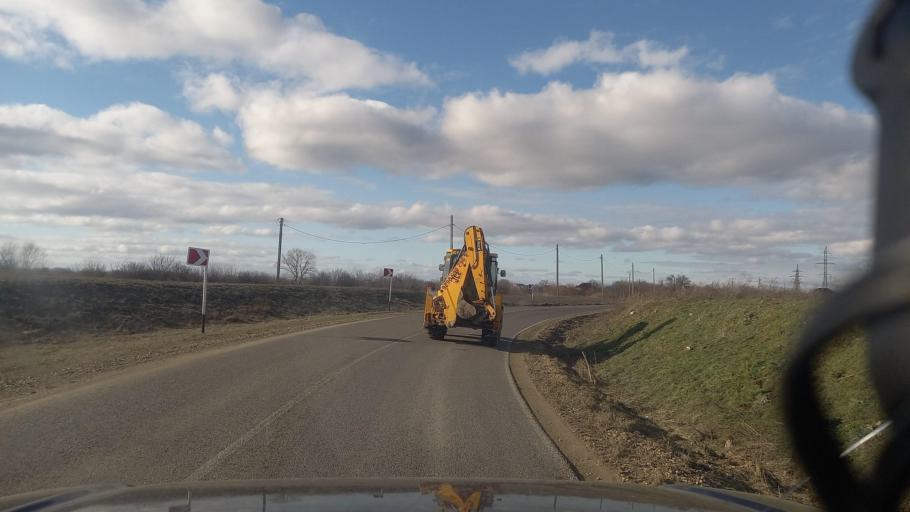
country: RU
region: Adygeya
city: Yablonovskiy
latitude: 45.0210
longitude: 38.8987
